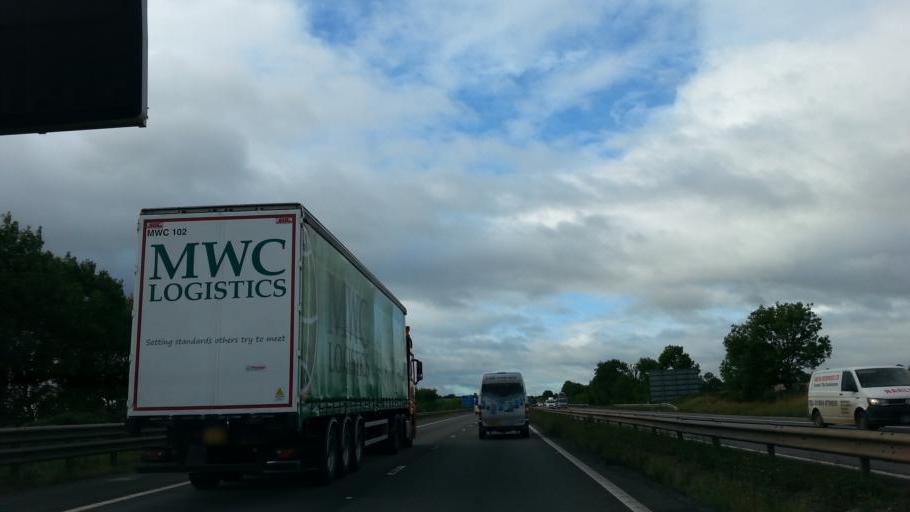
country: GB
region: England
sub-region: Derbyshire
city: Netherseal
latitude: 52.6805
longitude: -1.5529
